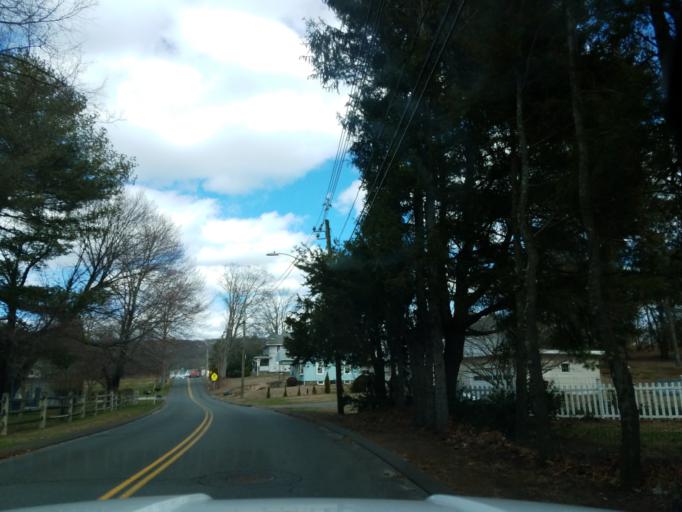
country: US
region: Connecticut
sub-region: New Haven County
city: Naugatuck
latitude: 41.4696
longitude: -73.0472
